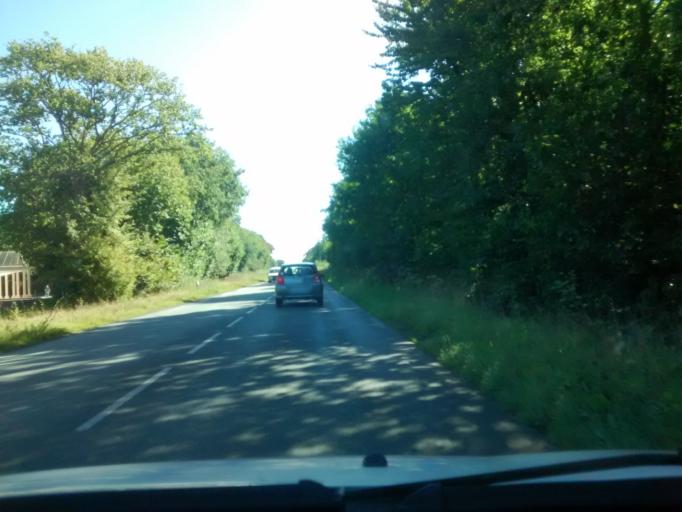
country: FR
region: Brittany
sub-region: Departement d'Ille-et-Vilaine
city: Saint-Briac-sur-Mer
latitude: 48.6150
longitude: -2.1131
